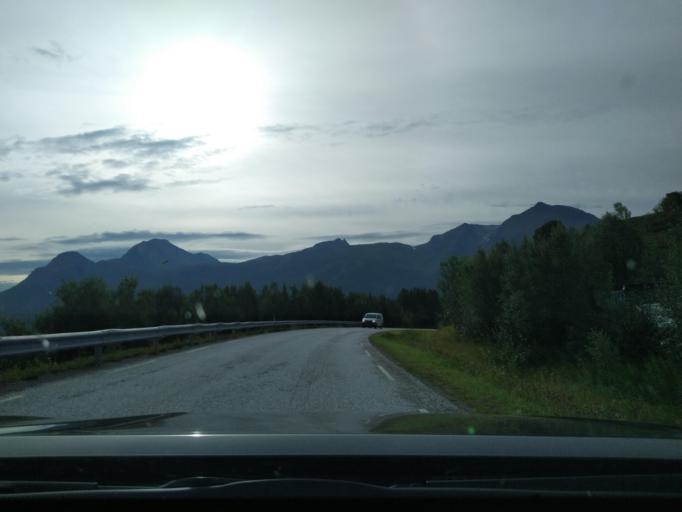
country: NO
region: Troms
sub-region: Dyroy
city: Brostadbotn
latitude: 68.8772
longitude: 17.4816
